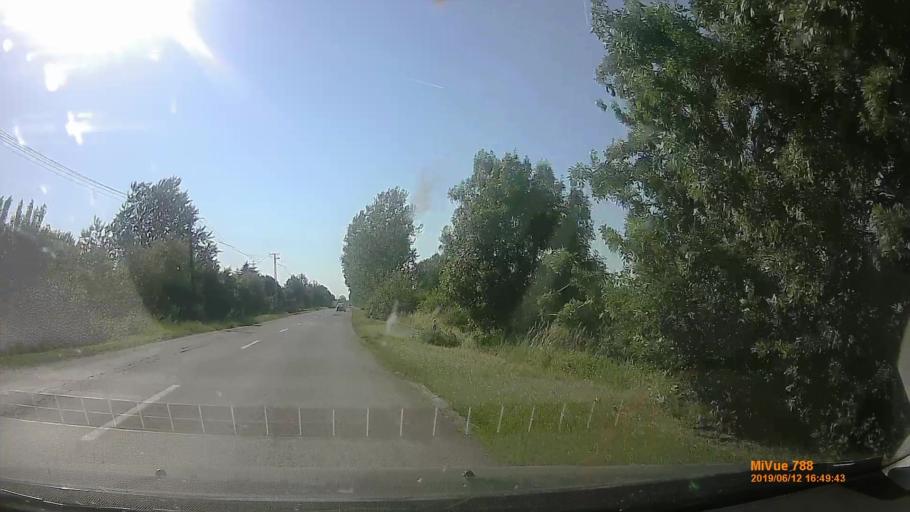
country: HU
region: Csongrad
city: Kiszombor
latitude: 46.1946
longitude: 20.4061
